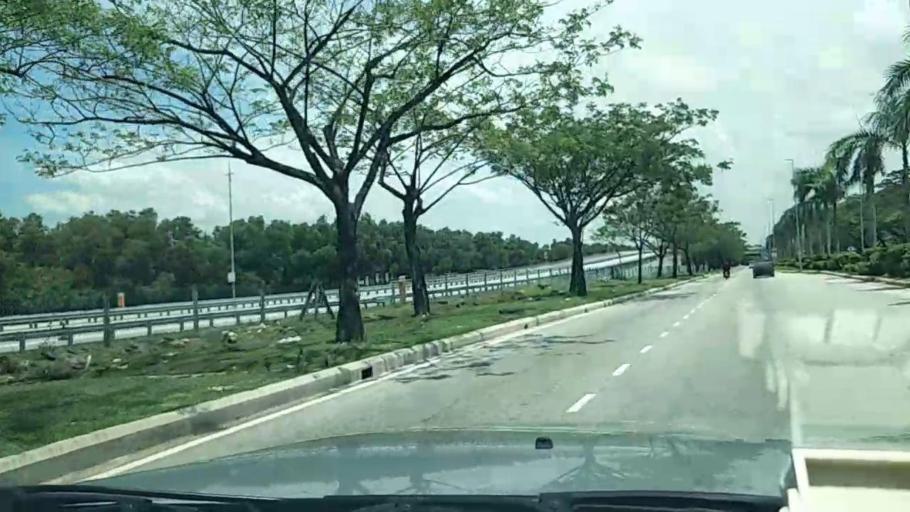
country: MY
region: Putrajaya
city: Putrajaya
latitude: 2.9555
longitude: 101.6170
